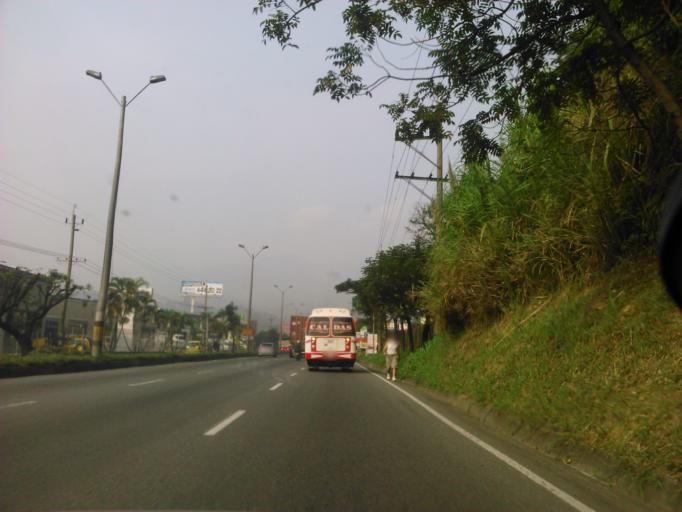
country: CO
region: Antioquia
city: Sabaneta
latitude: 6.1585
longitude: -75.6203
